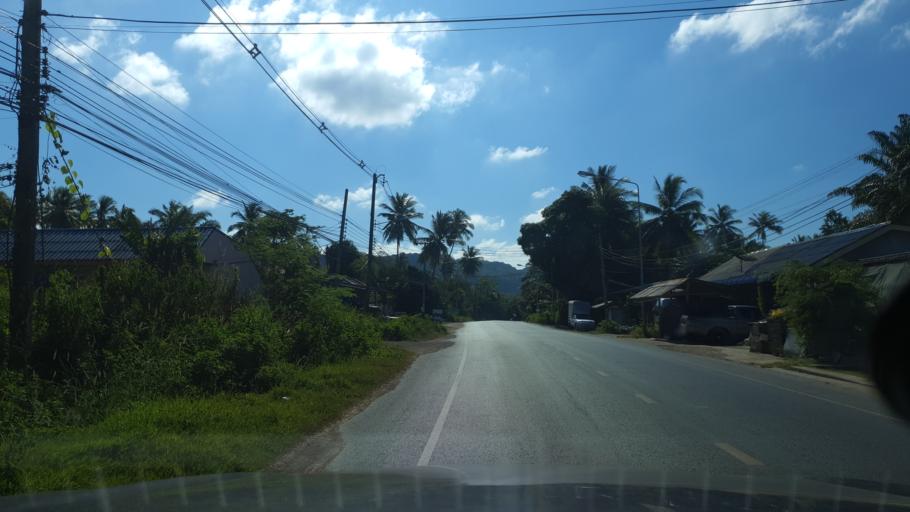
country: TH
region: Phangnga
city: Ban Ao Nang
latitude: 8.0624
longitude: 98.8123
